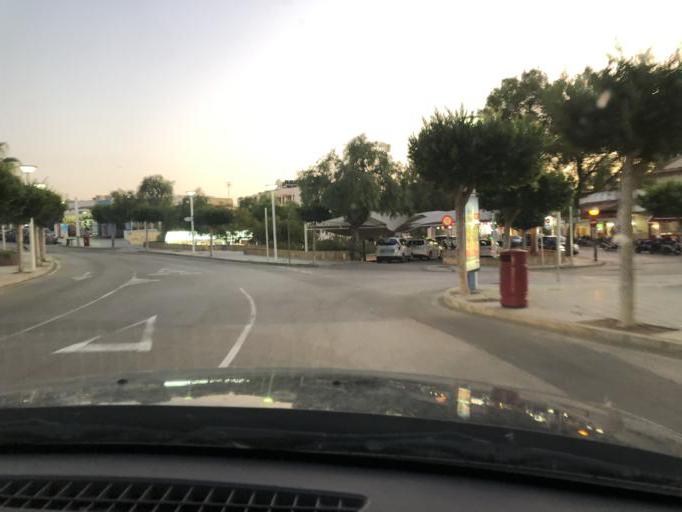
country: ES
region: Balearic Islands
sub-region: Illes Balears
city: Santa Ponsa
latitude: 39.5214
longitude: 2.4727
